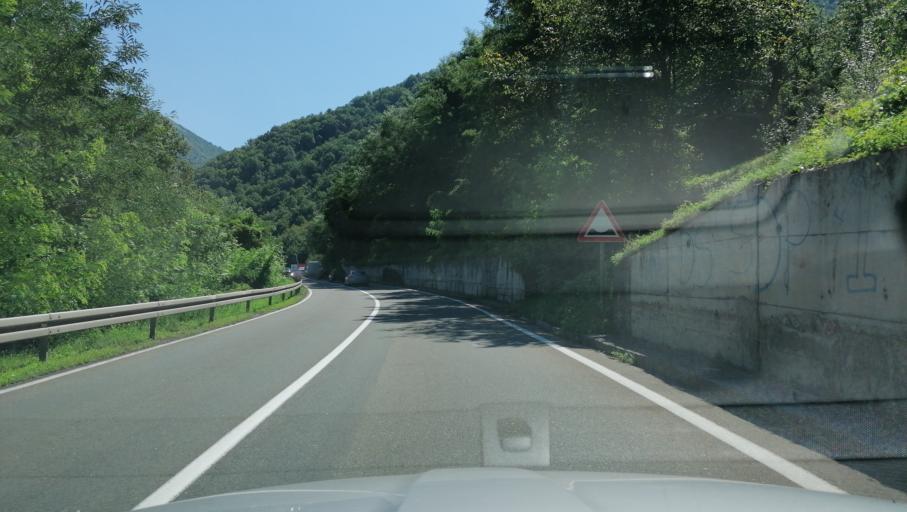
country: RS
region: Central Serbia
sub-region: Raski Okrug
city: Kraljevo
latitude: 43.6127
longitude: 20.5472
